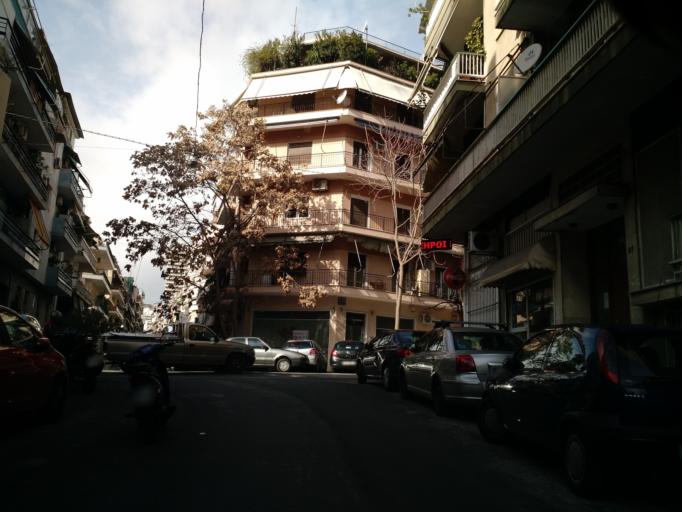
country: GR
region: Attica
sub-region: Nomarchia Athinas
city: Neo Psychiko
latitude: 37.9897
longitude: 23.7688
